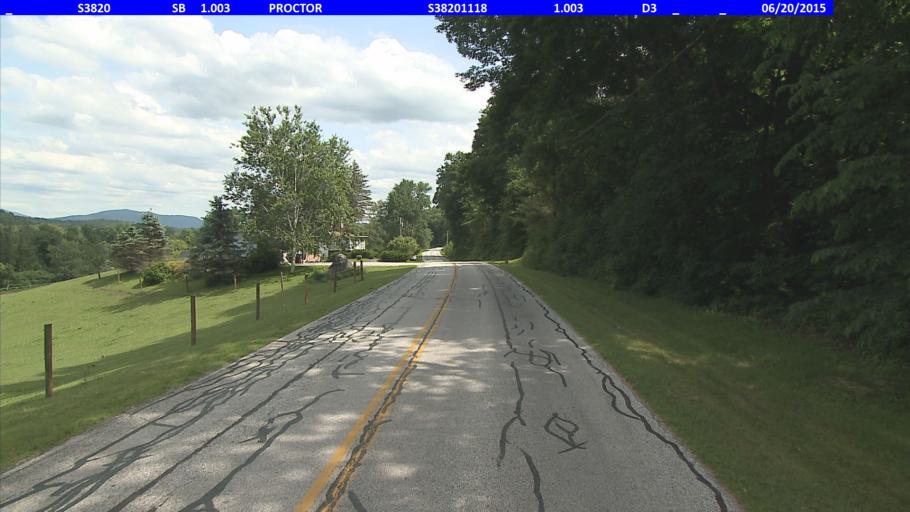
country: US
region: Vermont
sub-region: Rutland County
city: West Rutland
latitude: 43.6241
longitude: -73.0348
